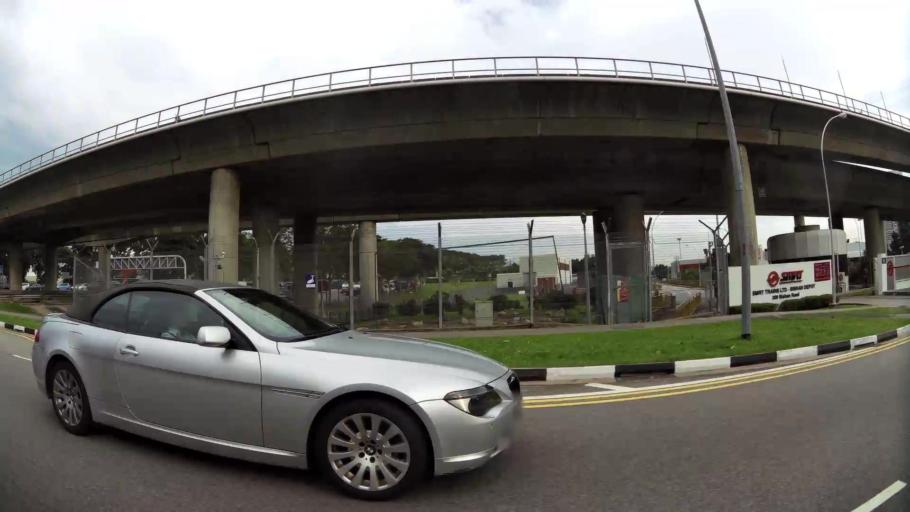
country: SG
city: Singapore
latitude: 1.3594
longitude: 103.8519
